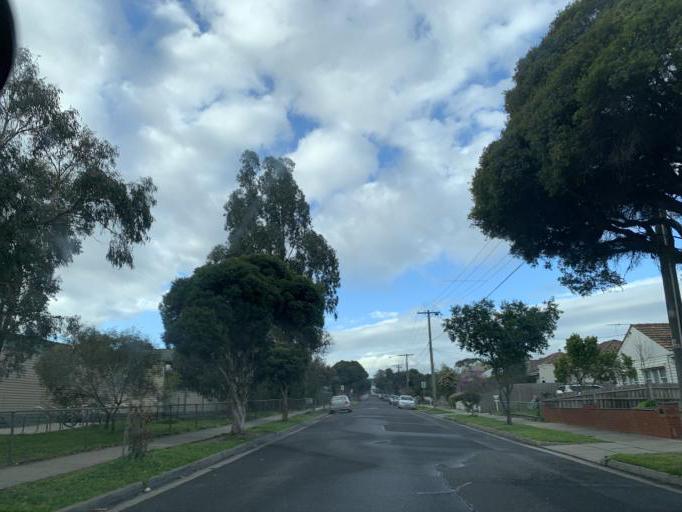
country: AU
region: Victoria
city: Thornbury
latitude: -37.7471
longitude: 144.9911
